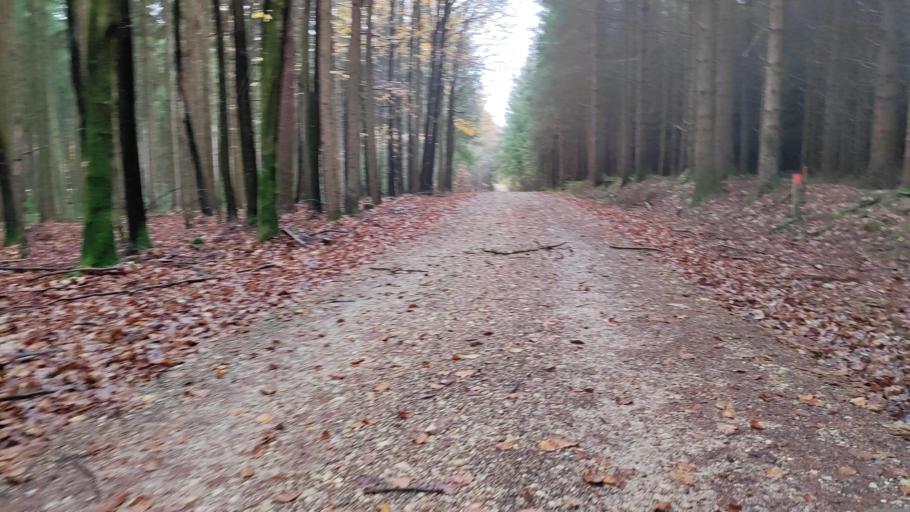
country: DE
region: Bavaria
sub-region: Swabia
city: Burtenbach
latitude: 48.3623
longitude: 10.5169
